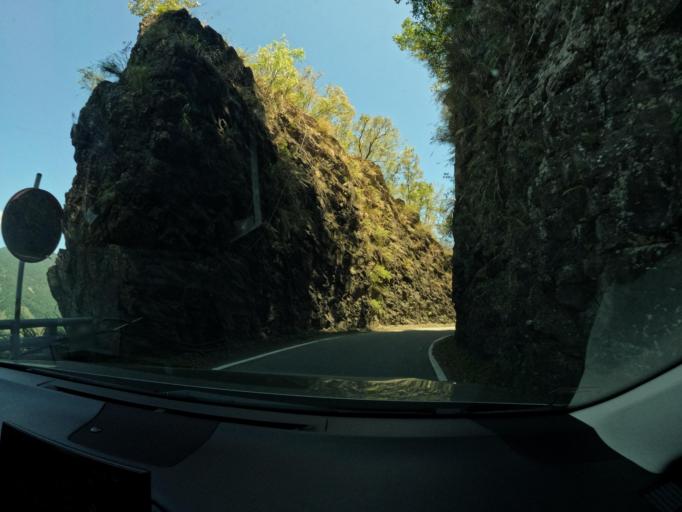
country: TW
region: Taiwan
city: Yujing
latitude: 23.2887
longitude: 120.8564
